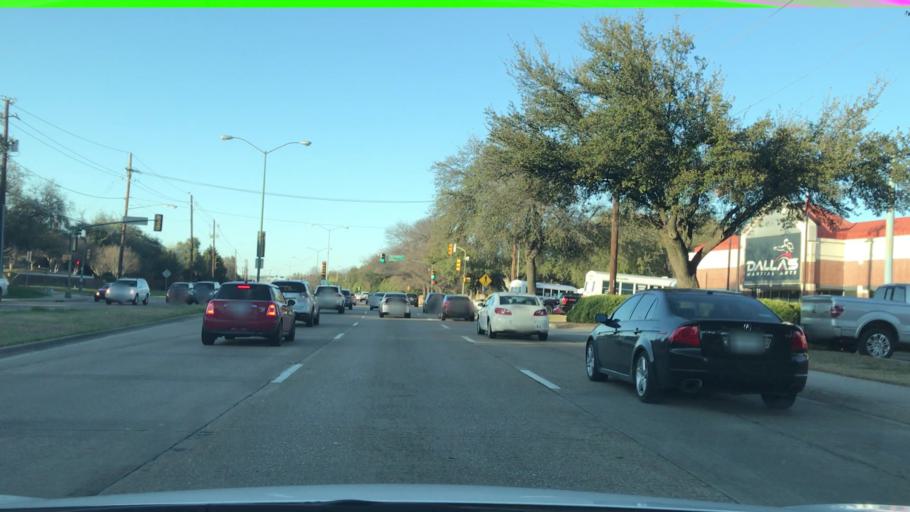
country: US
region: Texas
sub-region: Dallas County
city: Addison
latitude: 33.0018
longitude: -96.7961
